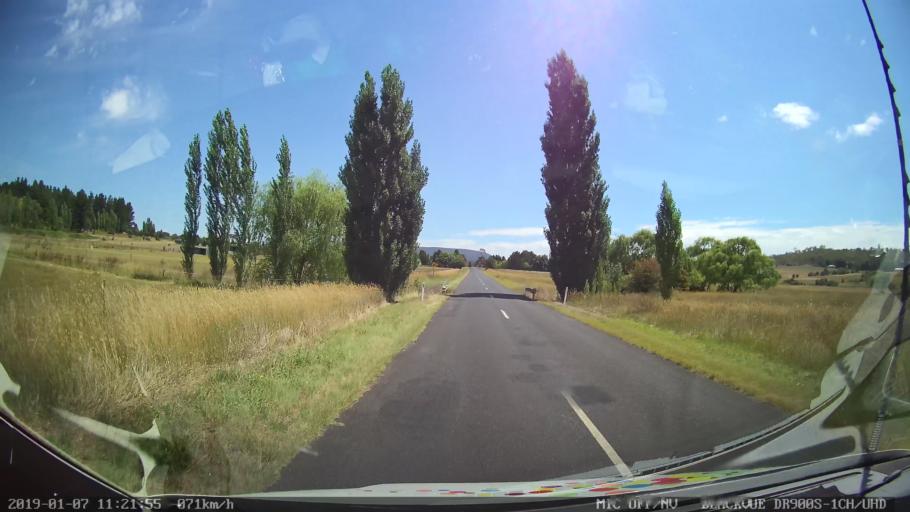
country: AU
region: New South Wales
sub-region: Armidale Dumaresq
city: Armidale
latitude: -30.4891
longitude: 151.6281
